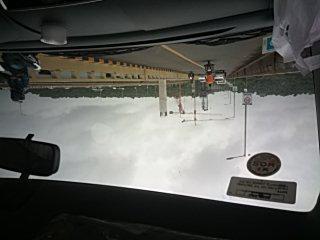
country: IN
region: Goa
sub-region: North Goa
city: Panaji
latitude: 15.5008
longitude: 73.8367
